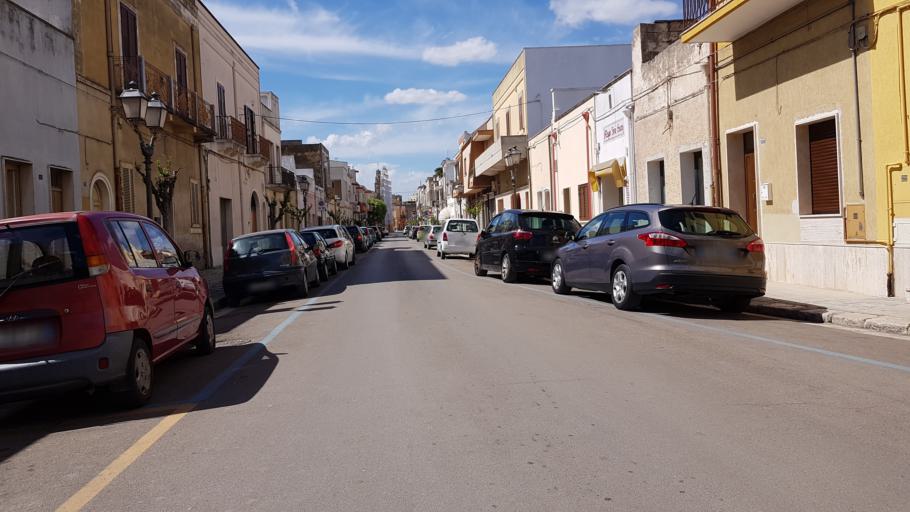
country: IT
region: Apulia
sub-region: Provincia di Brindisi
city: Mesagne
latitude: 40.5560
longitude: 17.8122
